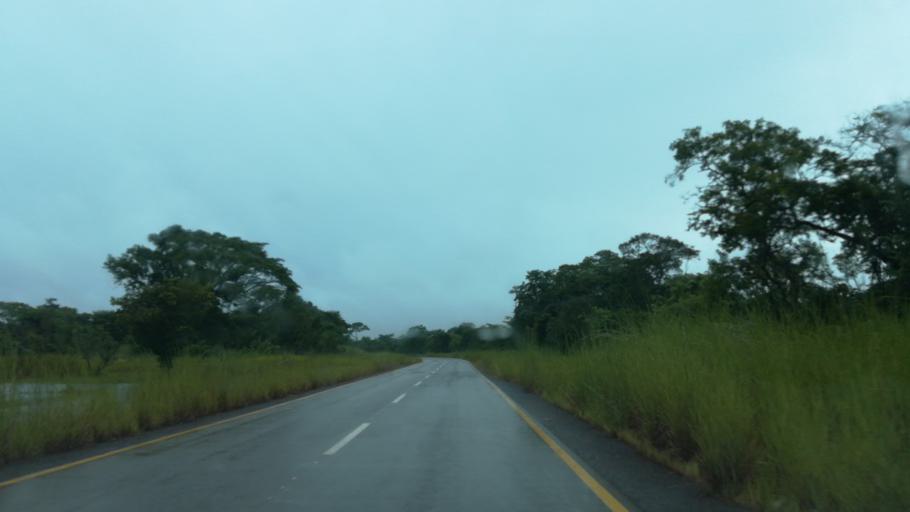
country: ZM
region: Luapula
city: Mwense
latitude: -10.8575
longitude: 28.2251
